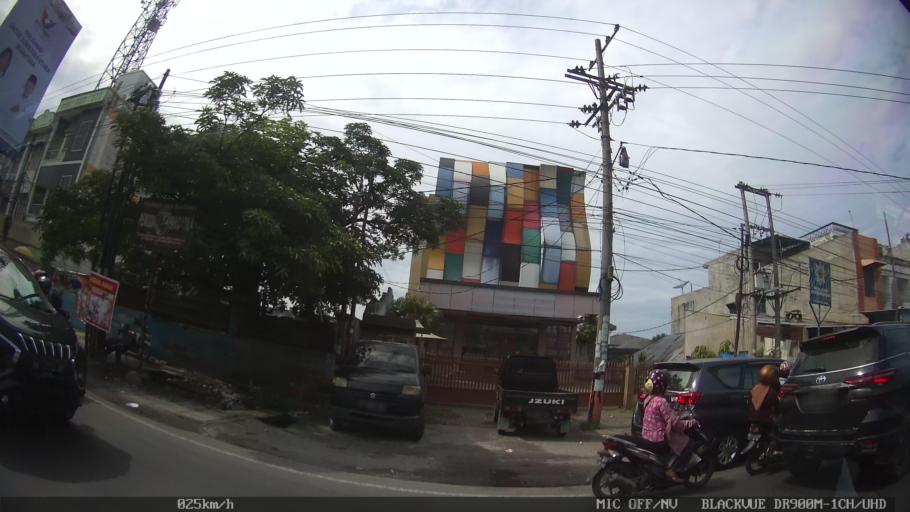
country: ID
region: North Sumatra
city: Sunggal
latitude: 3.5990
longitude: 98.6040
